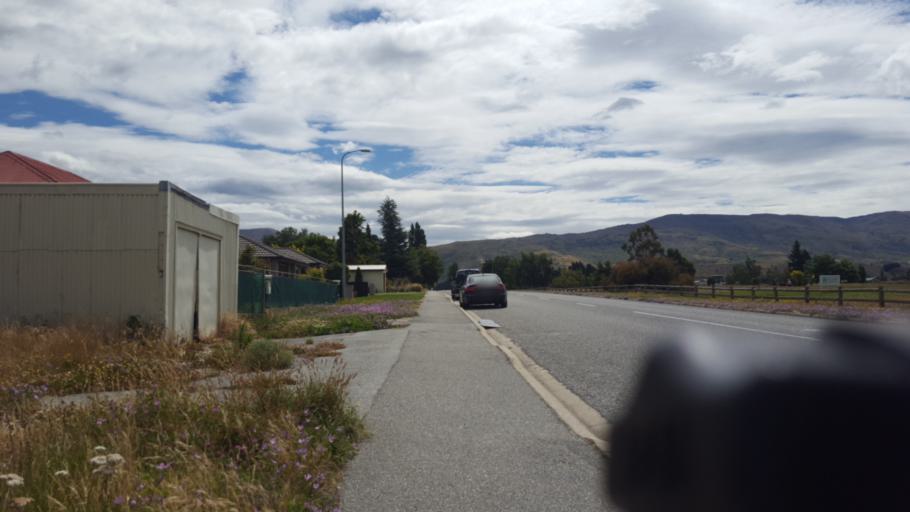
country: NZ
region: Otago
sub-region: Queenstown-Lakes District
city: Wanaka
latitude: -45.0424
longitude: 169.2138
